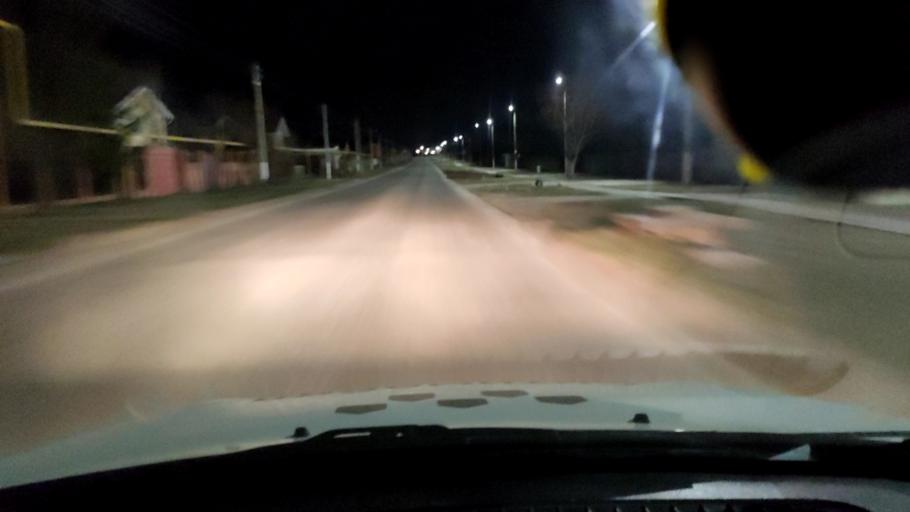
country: RU
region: Samara
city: Podstepki
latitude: 53.6159
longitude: 49.0454
